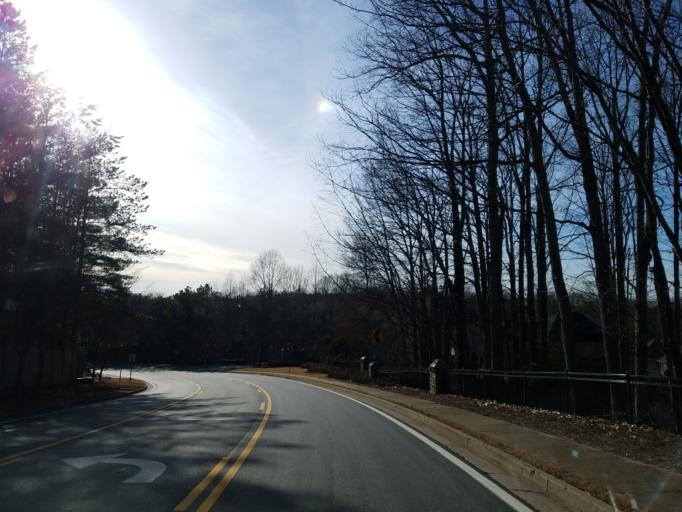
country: US
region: Georgia
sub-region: Cherokee County
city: Woodstock
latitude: 34.0407
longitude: -84.4649
